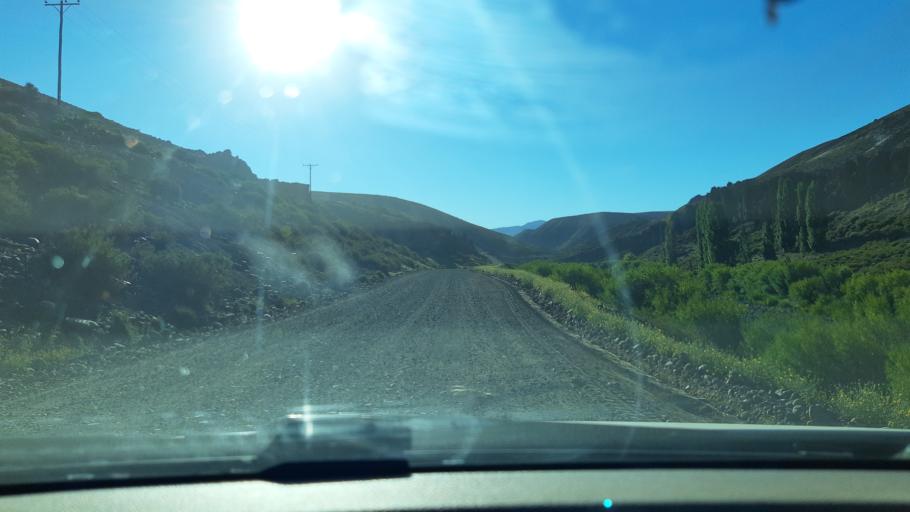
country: AR
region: Neuquen
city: Las Ovejas
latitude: -36.8099
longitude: -70.7102
